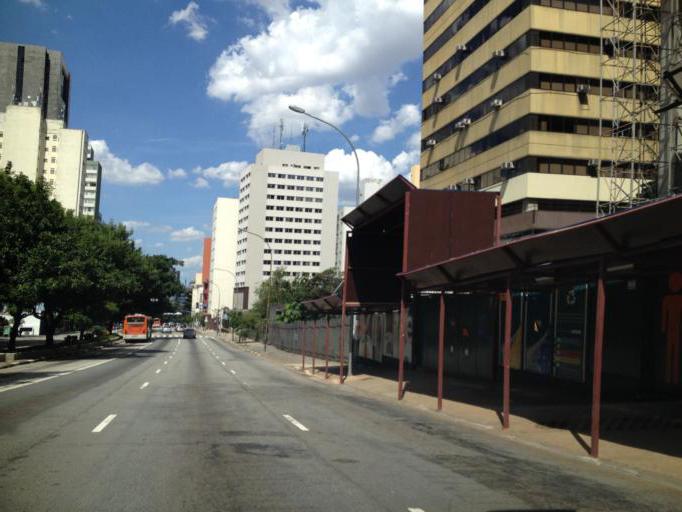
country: BR
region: Sao Paulo
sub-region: Sao Paulo
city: Sao Paulo
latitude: -23.5509
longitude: -46.6554
